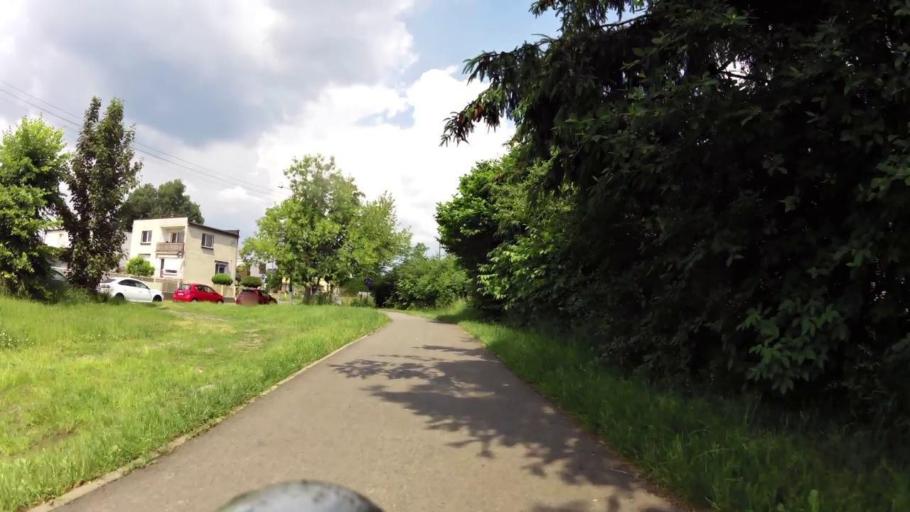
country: PL
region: Kujawsko-Pomorskie
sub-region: Powiat bydgoski
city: Koronowo
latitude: 53.3052
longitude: 17.9458
